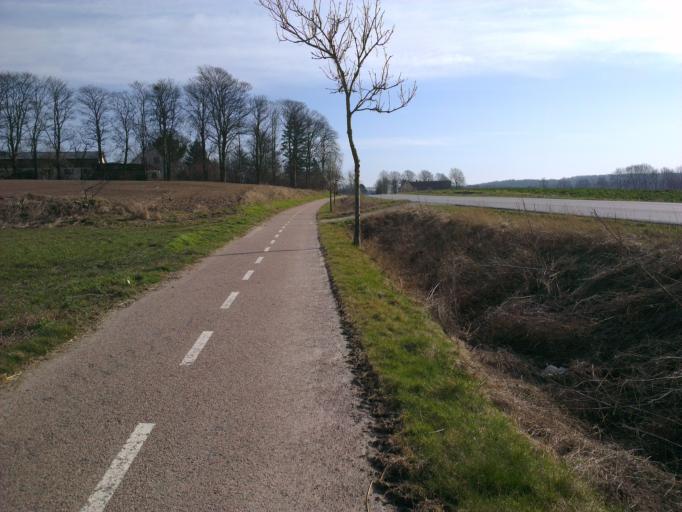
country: DK
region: Capital Region
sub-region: Frederikssund Kommune
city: Skibby
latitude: 55.7924
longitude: 11.9354
